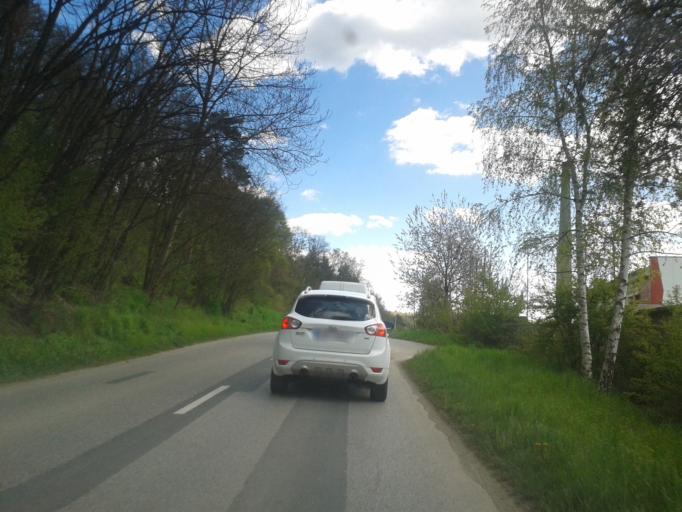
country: CZ
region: Central Bohemia
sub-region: Okres Beroun
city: Beroun
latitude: 49.9839
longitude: 14.0716
